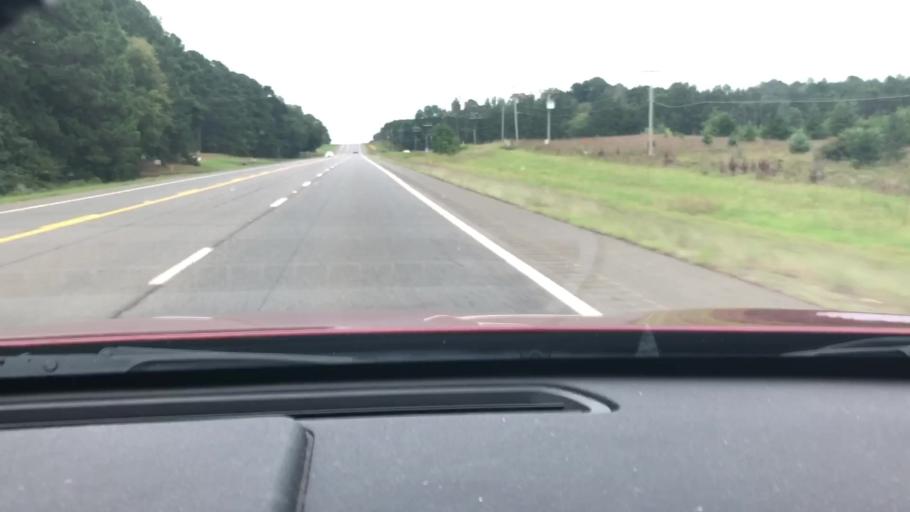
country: US
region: Arkansas
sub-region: Lafayette County
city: Stamps
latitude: 33.3630
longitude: -93.4651
